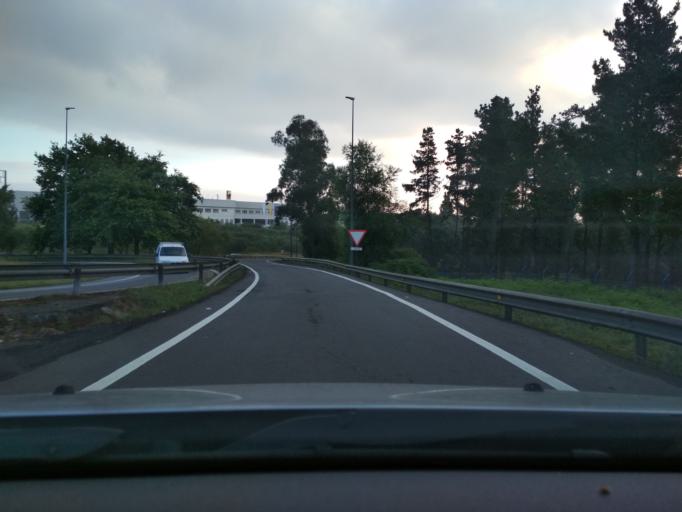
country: ES
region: Galicia
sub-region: Provincia da Coruna
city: Santiago de Compostela
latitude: 42.9081
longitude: -8.5091
